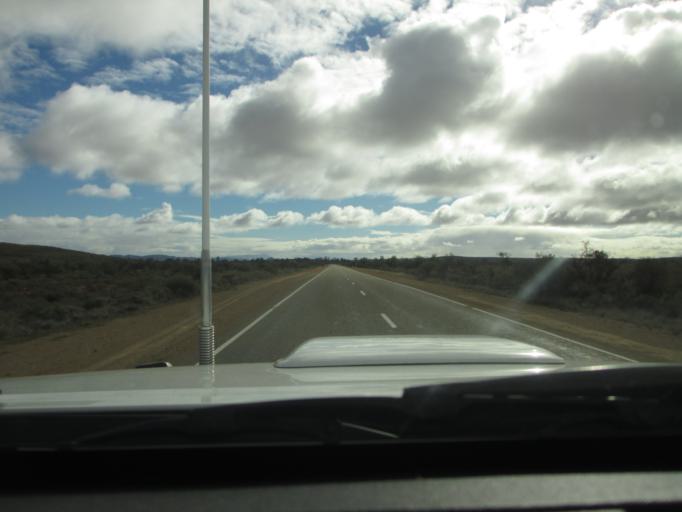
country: AU
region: South Australia
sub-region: Flinders Ranges
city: Quorn
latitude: -32.0874
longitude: 138.5029
